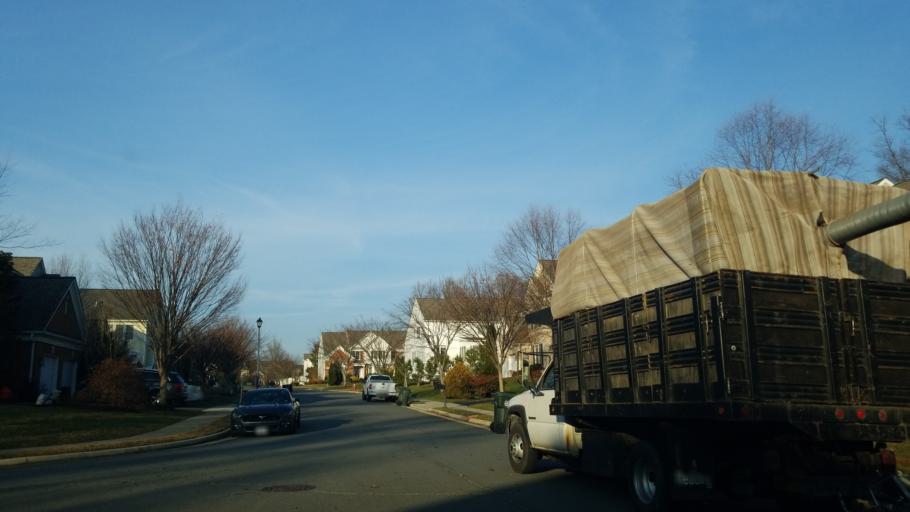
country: US
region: Virginia
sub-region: Fairfax County
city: Greenbriar
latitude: 38.8501
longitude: -77.3934
